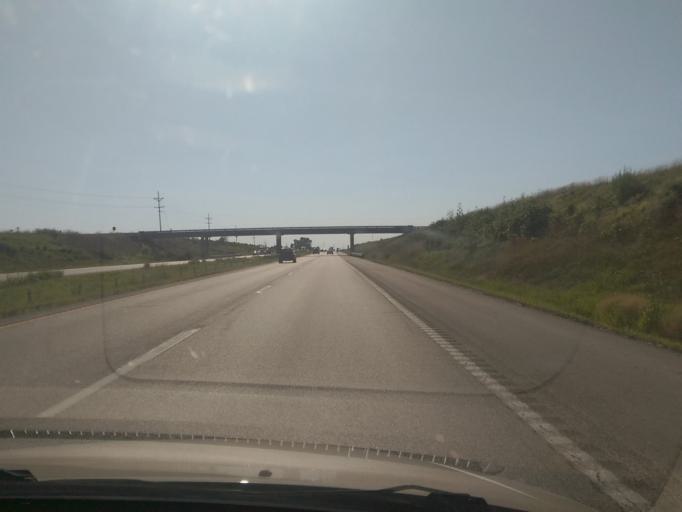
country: US
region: Missouri
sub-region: Saline County
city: Sweet Springs
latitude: 38.9787
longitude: -93.4565
